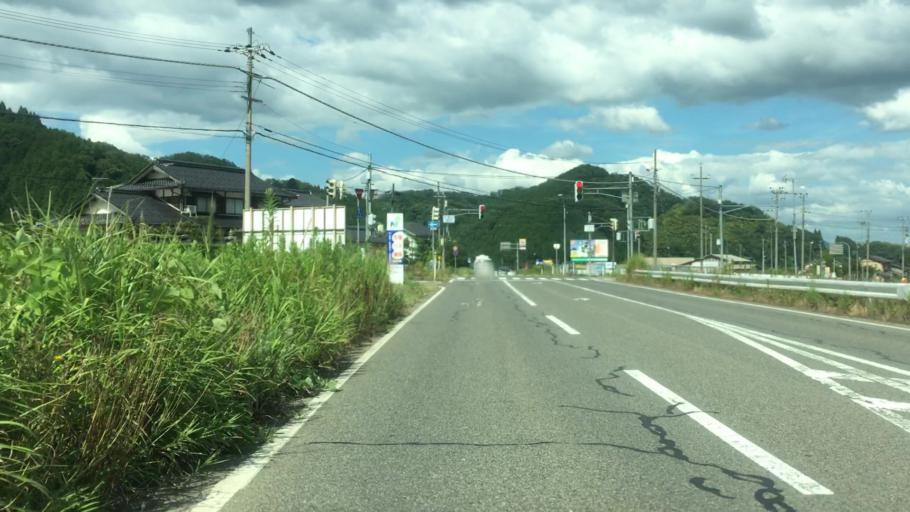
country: JP
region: Hyogo
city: Toyooka
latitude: 35.4634
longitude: 134.7418
